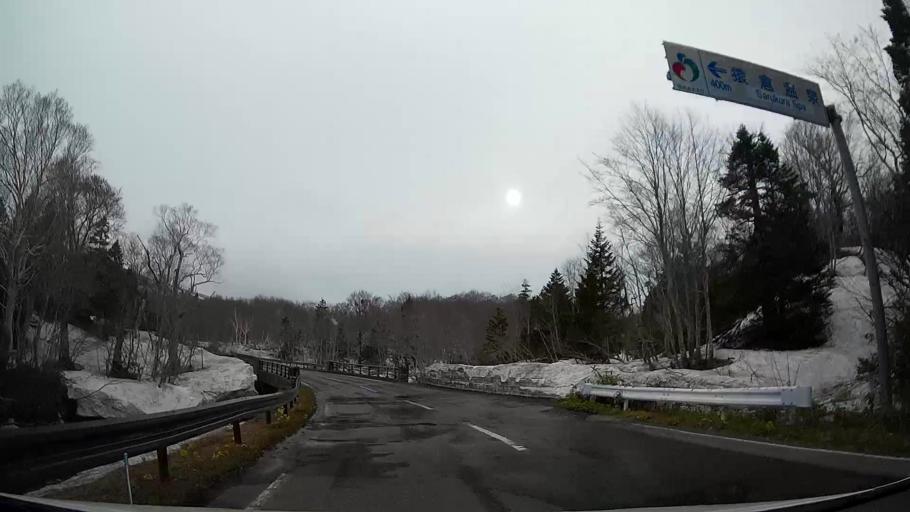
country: JP
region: Aomori
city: Aomori Shi
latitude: 40.6317
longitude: 140.9102
